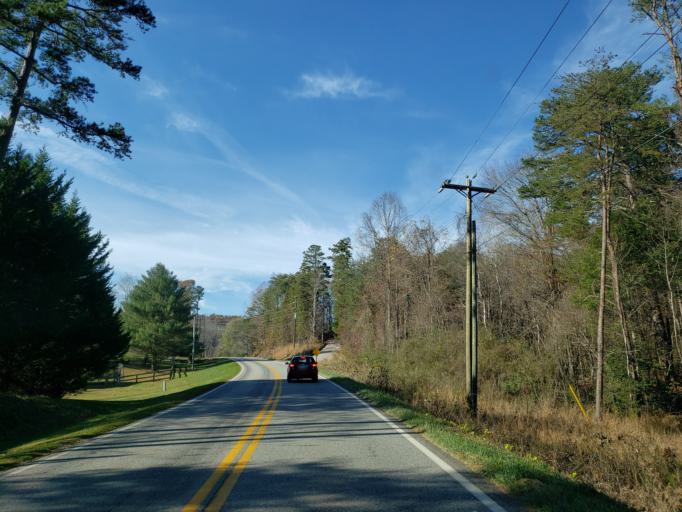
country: US
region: Georgia
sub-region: Lumpkin County
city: Dahlonega
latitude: 34.4562
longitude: -83.9993
